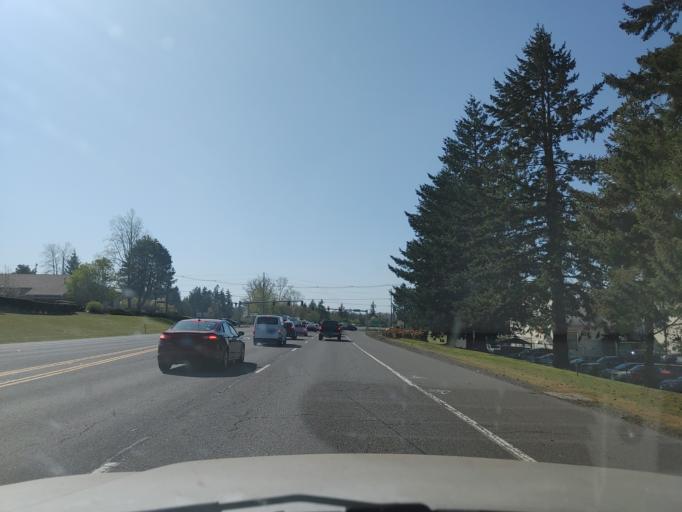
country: US
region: Oregon
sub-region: Clackamas County
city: Oatfield
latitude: 45.4243
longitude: -122.5908
